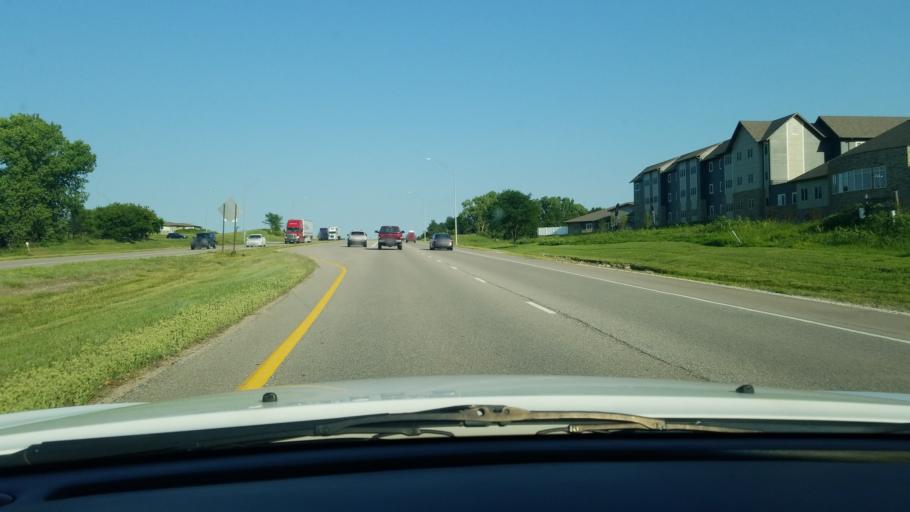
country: US
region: Nebraska
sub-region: Lancaster County
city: Lincoln
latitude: 40.7410
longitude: -96.6161
